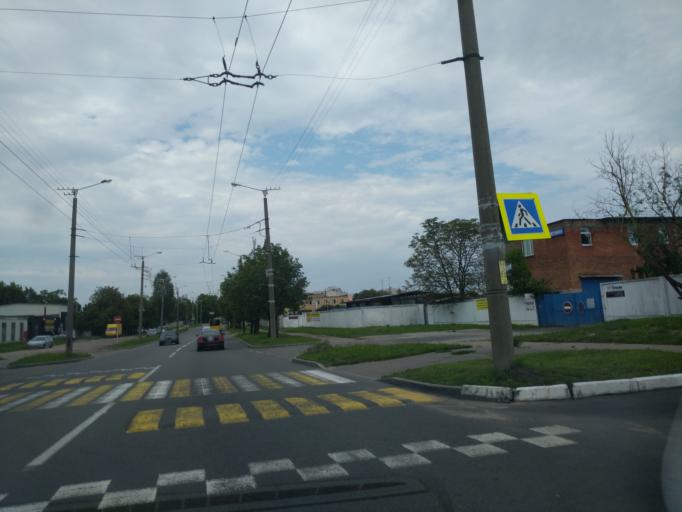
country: BY
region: Minsk
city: Novoye Medvezhino
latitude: 53.8864
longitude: 27.4809
